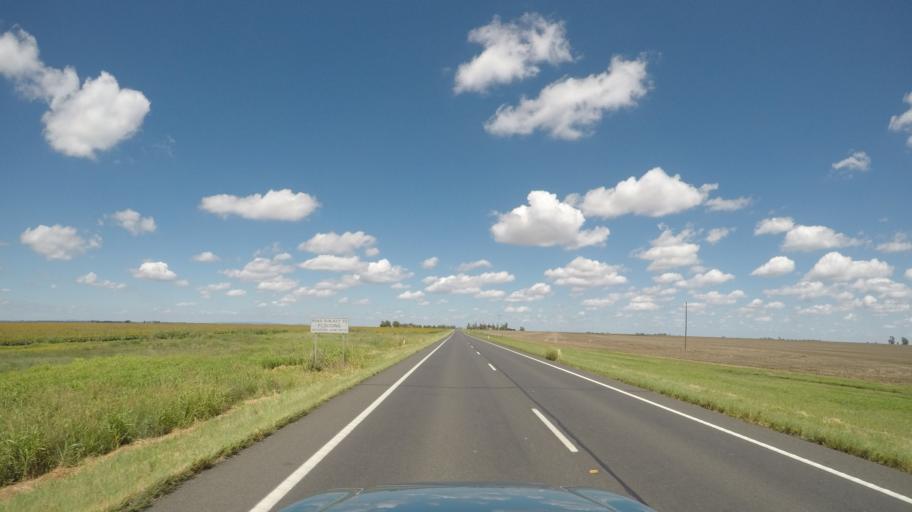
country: AU
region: Queensland
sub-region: Toowoomba
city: Westbrook
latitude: -27.7565
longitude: 151.5044
